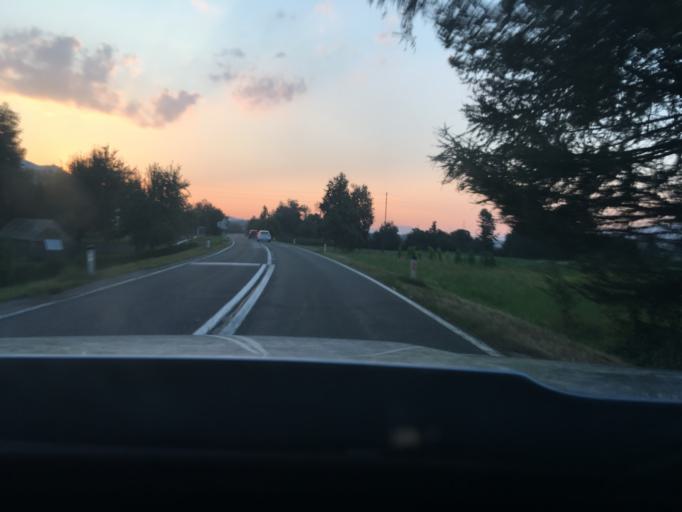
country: SI
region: Ribnica
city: Ribnica
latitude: 45.7091
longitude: 14.7562
